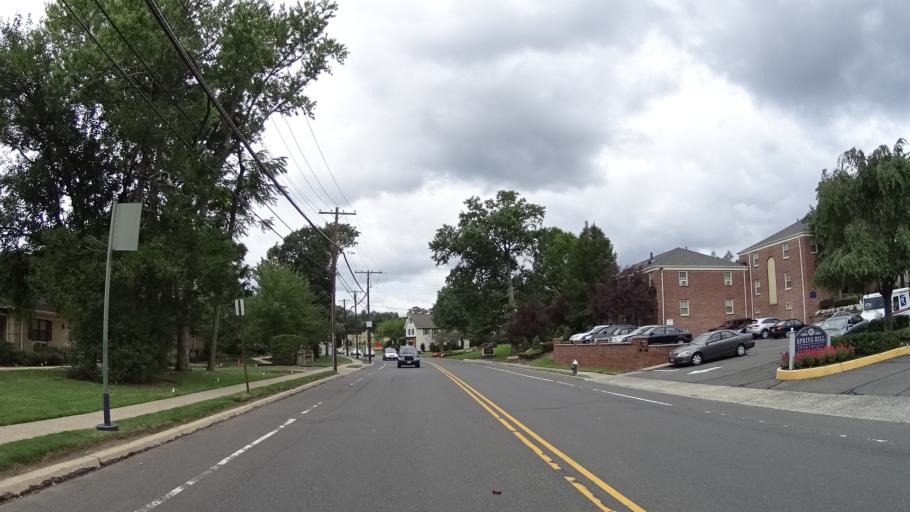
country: US
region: New Jersey
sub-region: Union County
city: New Providence
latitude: 40.7122
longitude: -74.3827
